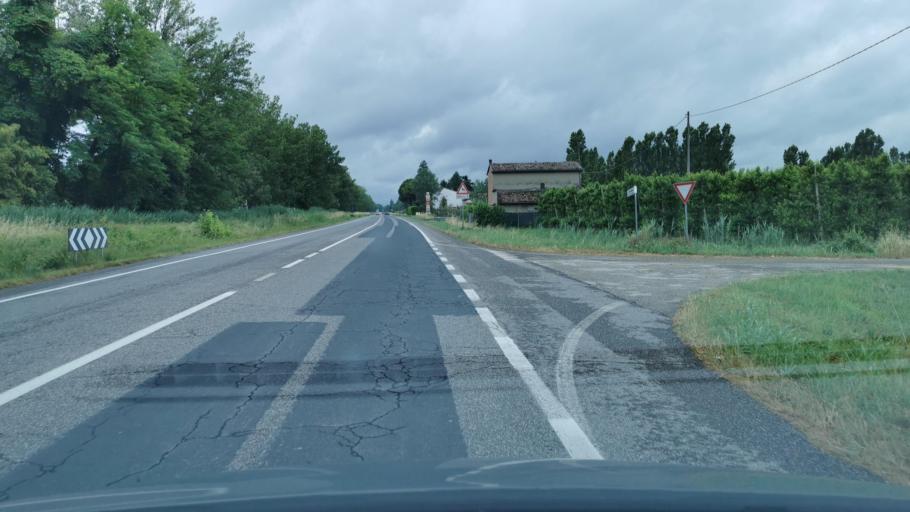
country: IT
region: Emilia-Romagna
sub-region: Provincia di Ravenna
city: Cotignola
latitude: 44.3967
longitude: 11.9594
